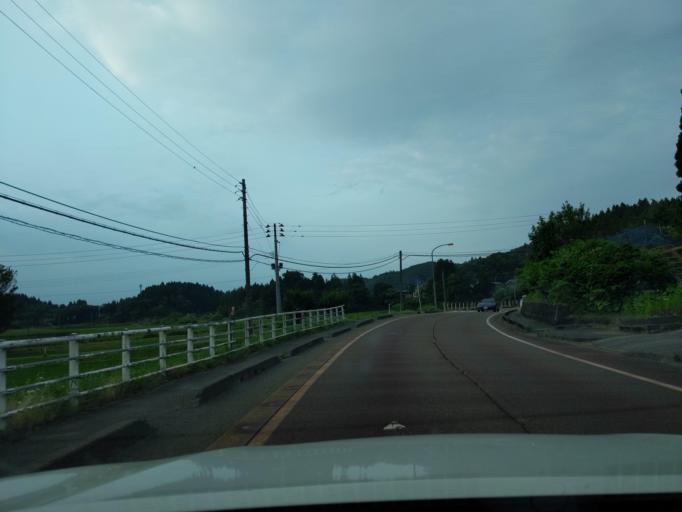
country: JP
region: Niigata
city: Nagaoka
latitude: 37.4348
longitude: 138.7255
